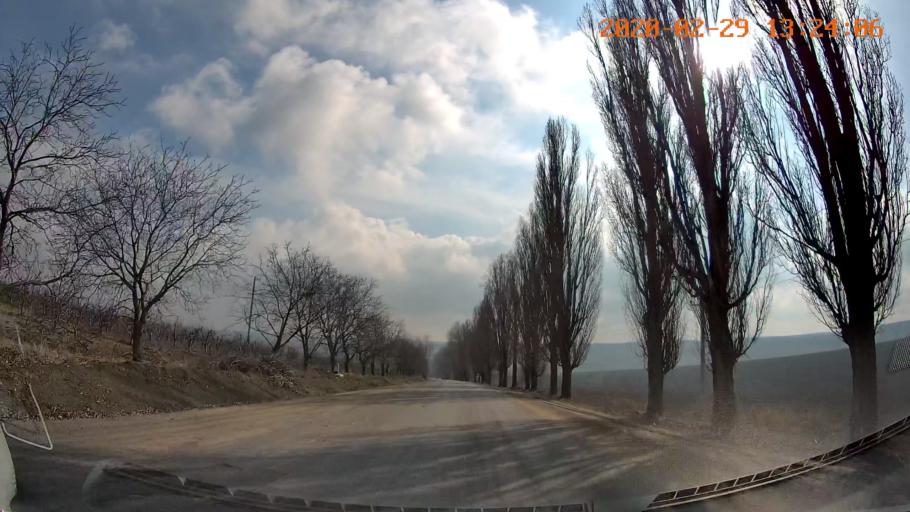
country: MD
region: Telenesti
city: Camenca
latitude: 47.9425
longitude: 28.6259
